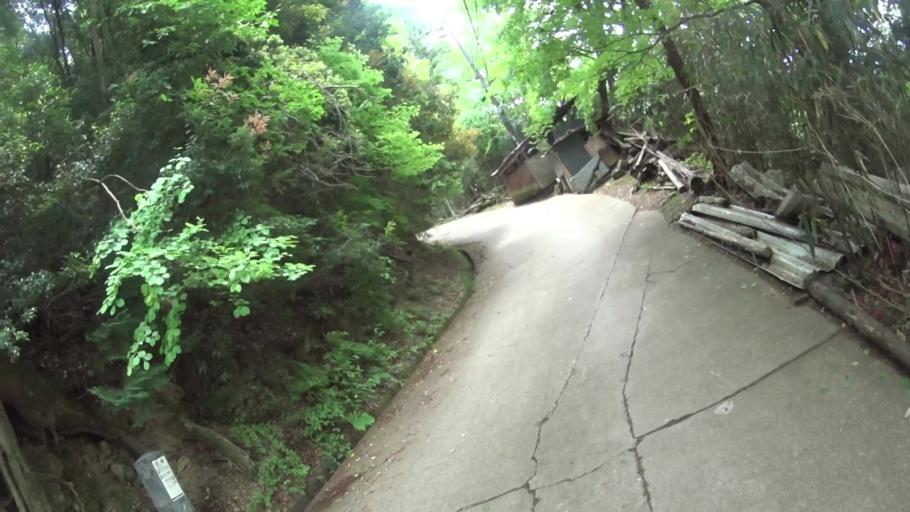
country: JP
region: Nara
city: Yoshino-cho
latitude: 34.3539
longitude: 135.8728
